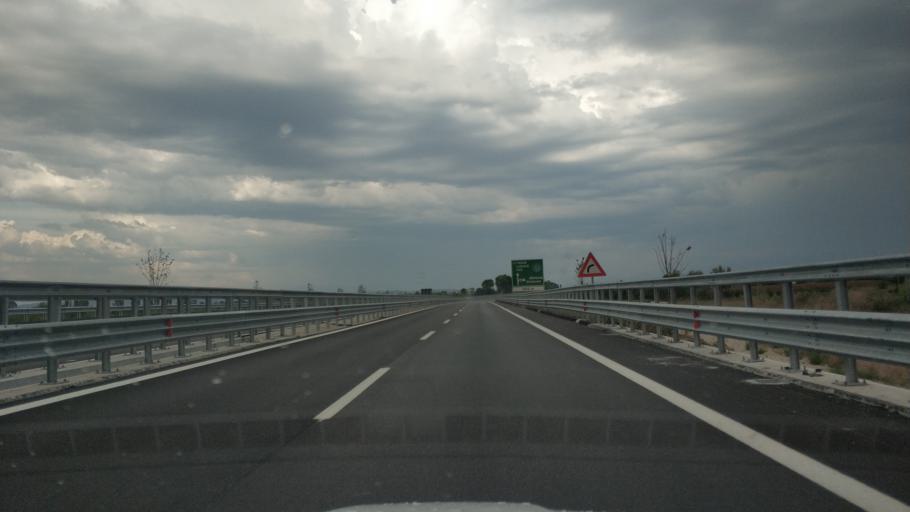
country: AL
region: Fier
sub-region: Rrethi i Fierit
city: Dermenas
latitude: 40.7396
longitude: 19.4693
